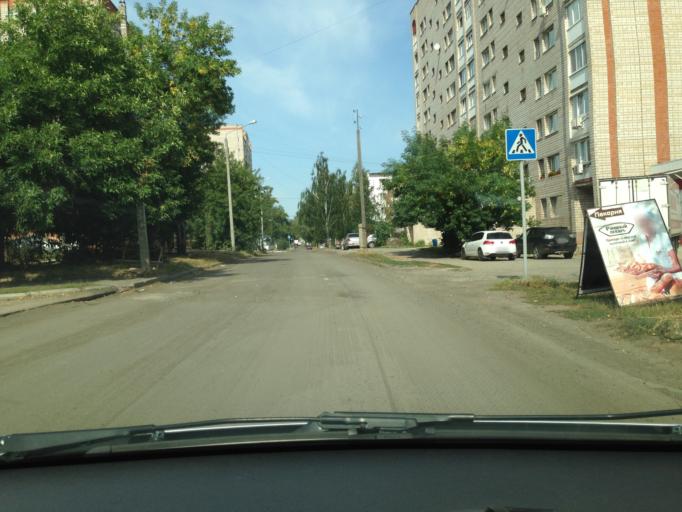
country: RU
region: Udmurtiya
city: Izhevsk
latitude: 56.8703
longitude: 53.1898
